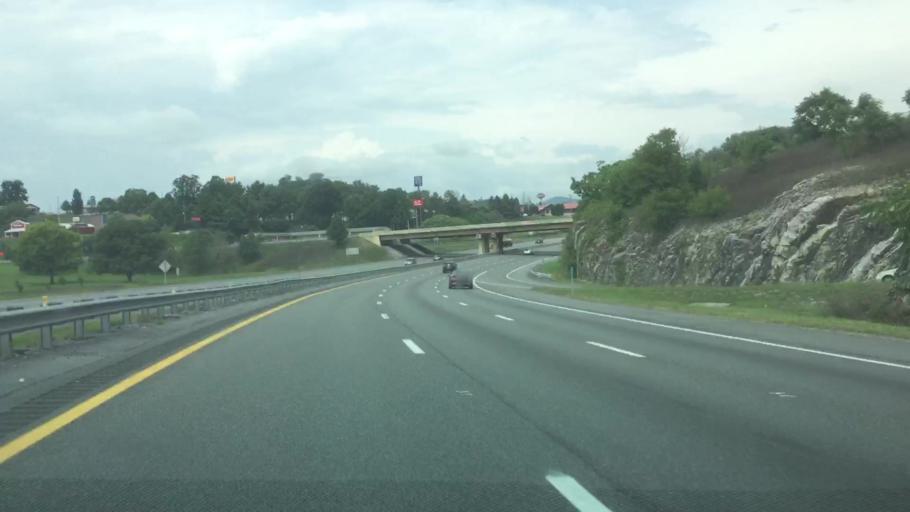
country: US
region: Virginia
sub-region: Wythe County
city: Wytheville
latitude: 36.9481
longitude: -81.0500
